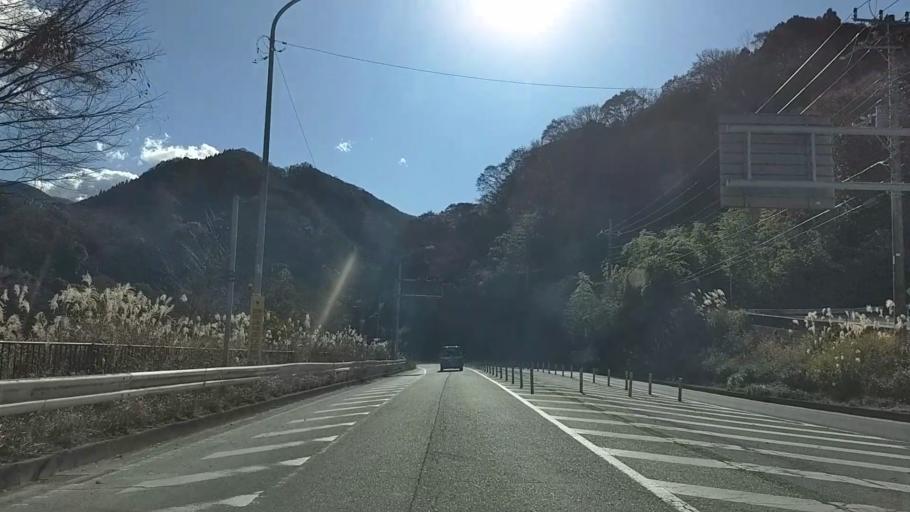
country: JP
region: Shizuoka
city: Gotemba
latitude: 35.3655
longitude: 139.0180
